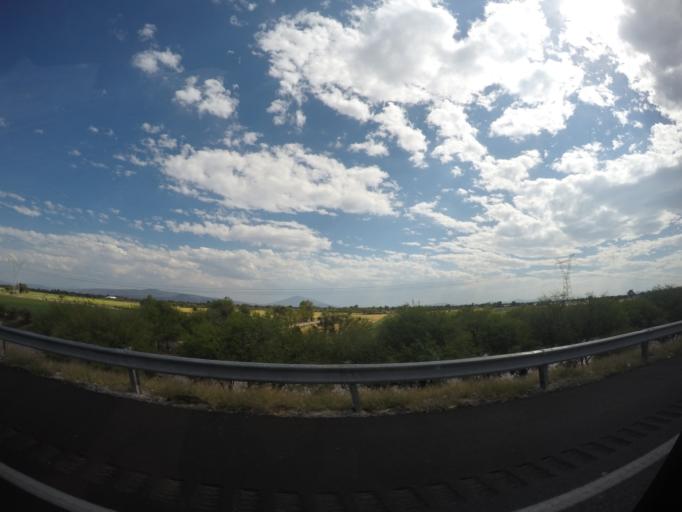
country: MX
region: Guanajuato
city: Santiago de Cuenda
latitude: 20.5793
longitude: -100.9774
